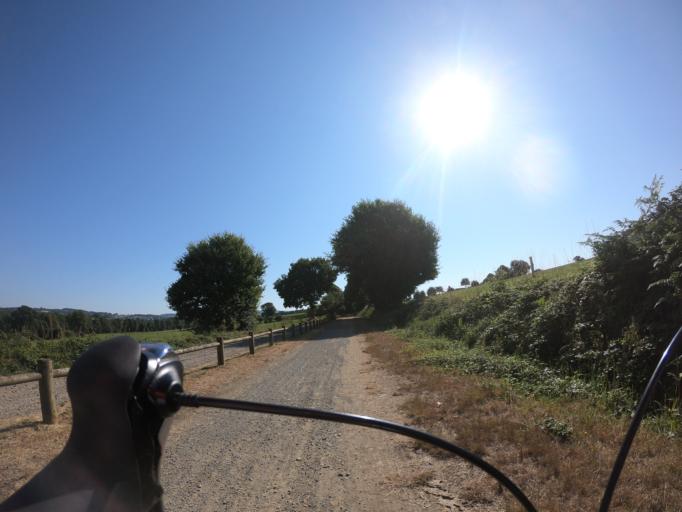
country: FR
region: Lower Normandy
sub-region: Departement de la Manche
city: Romagny
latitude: 48.6213
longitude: -0.9857
